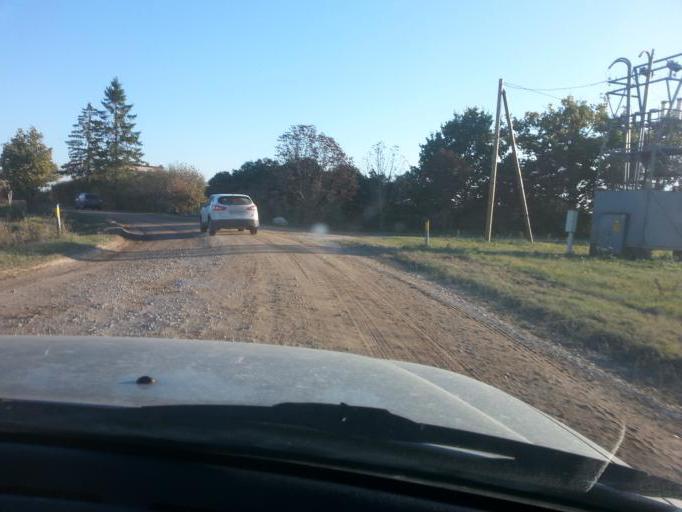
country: LV
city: Tervete
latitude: 56.6192
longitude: 23.4655
